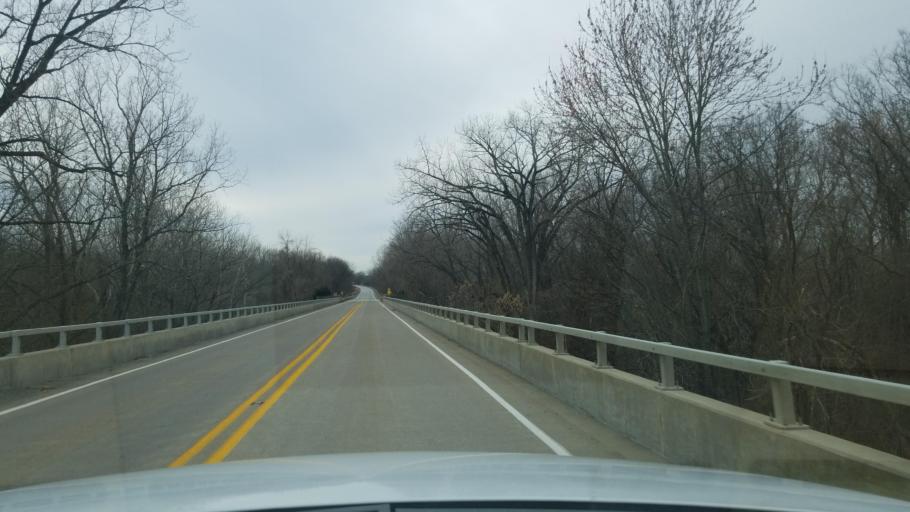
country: US
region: Indiana
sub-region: Posey County
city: Mount Vernon
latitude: 37.9440
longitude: -88.0385
